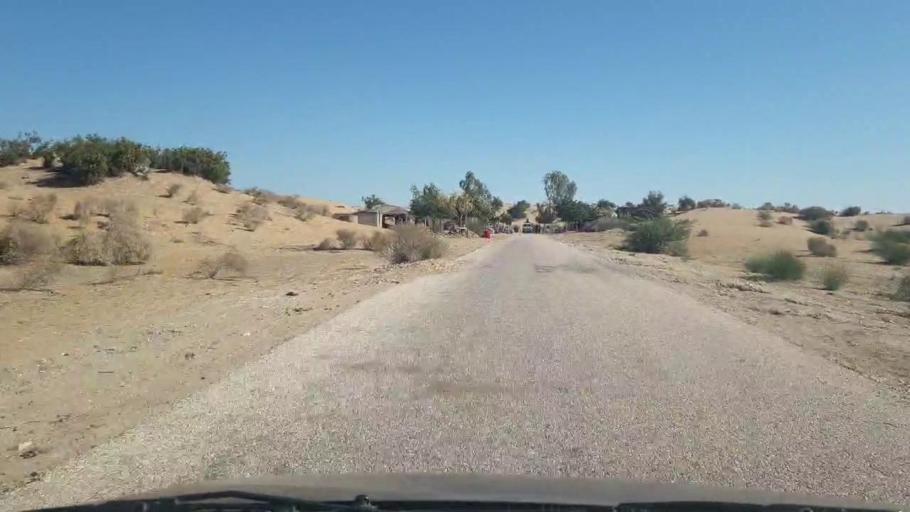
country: PK
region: Sindh
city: Bozdar
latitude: 27.0060
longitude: 68.9073
